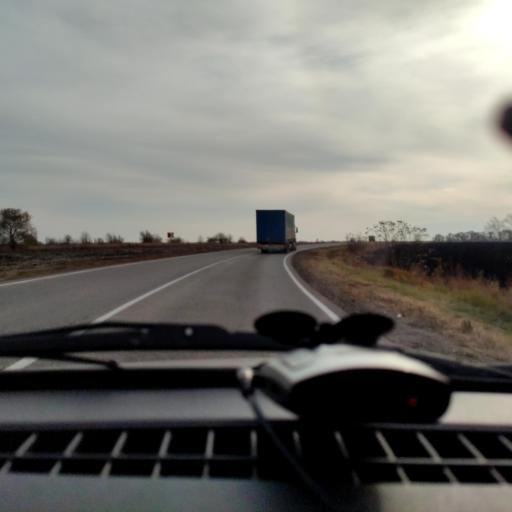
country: RU
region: Voronezj
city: Shilovo
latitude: 51.4658
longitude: 38.9663
